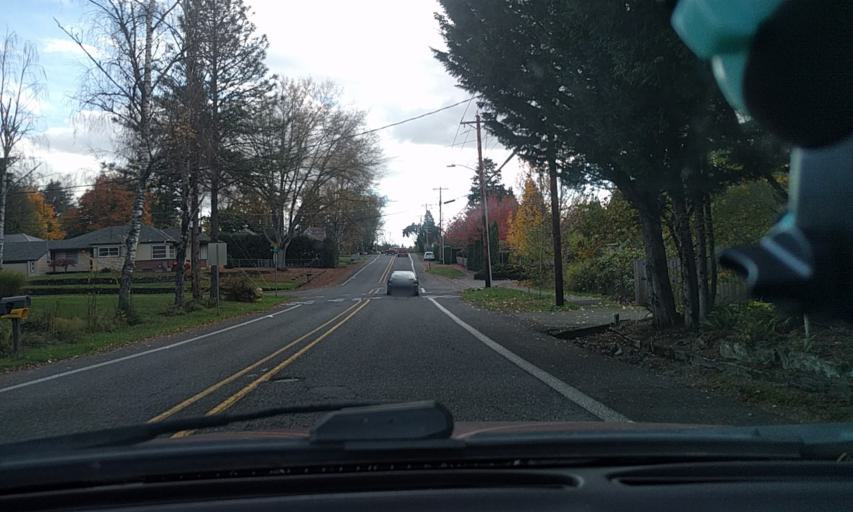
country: US
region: Oregon
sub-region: Washington County
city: West Slope
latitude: 45.4905
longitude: -122.7708
